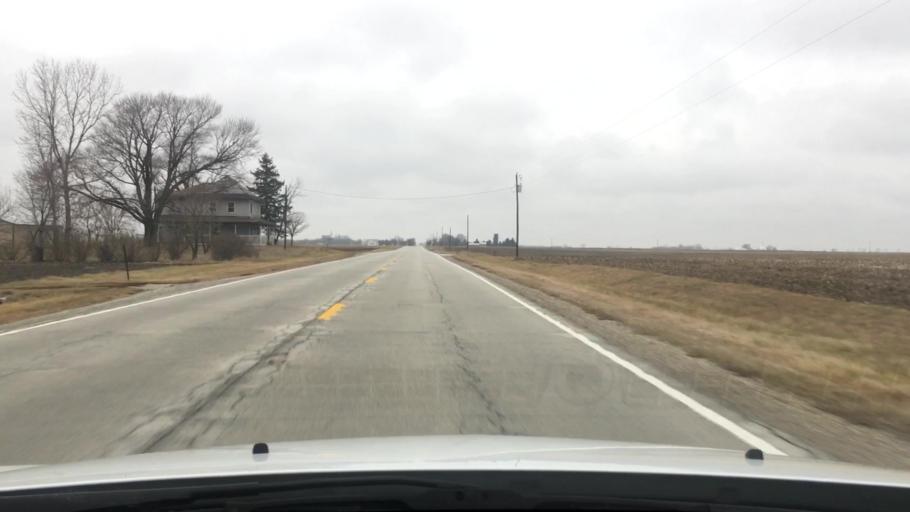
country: US
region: Illinois
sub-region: Iroquois County
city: Clifton
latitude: 40.8858
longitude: -87.9148
